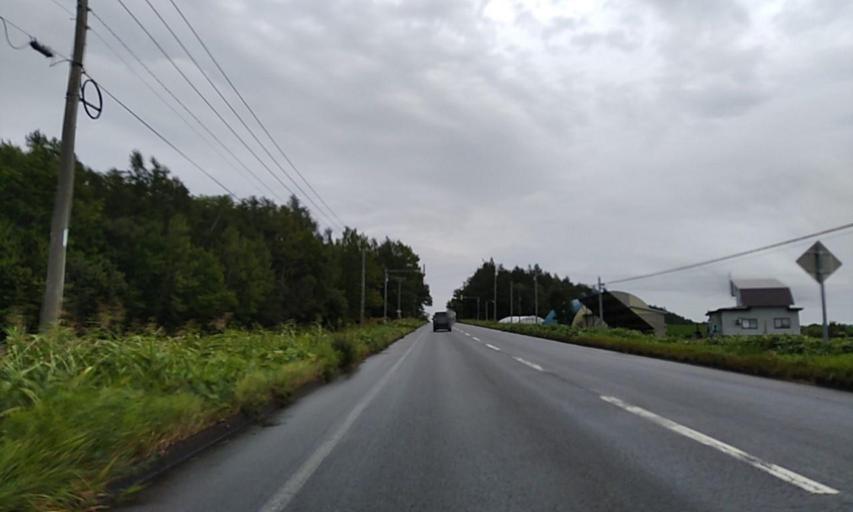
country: JP
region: Hokkaido
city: Abashiri
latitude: 44.1029
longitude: 143.9705
